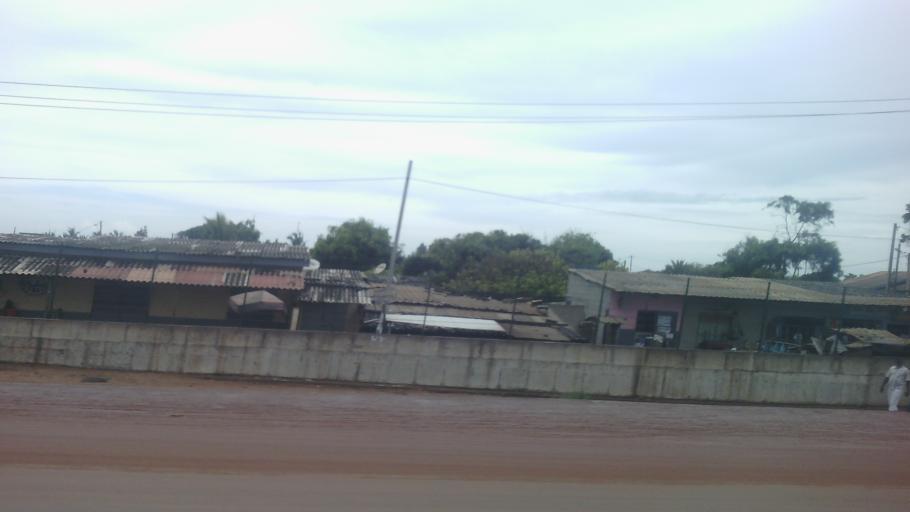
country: CI
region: Lagunes
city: Bingerville
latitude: 5.2395
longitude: -3.8969
